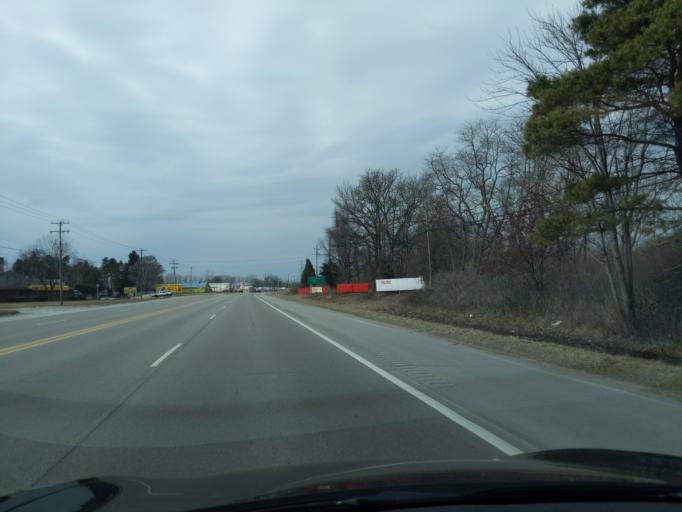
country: US
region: Michigan
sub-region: Bay County
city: Bay City
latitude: 43.6550
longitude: -83.9454
